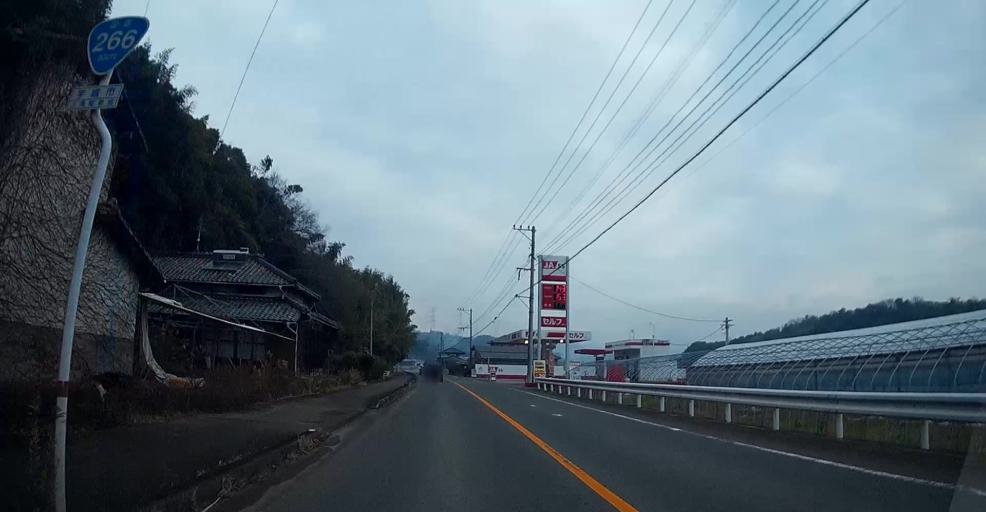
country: JP
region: Kumamoto
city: Yatsushiro
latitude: 32.6222
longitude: 130.5149
